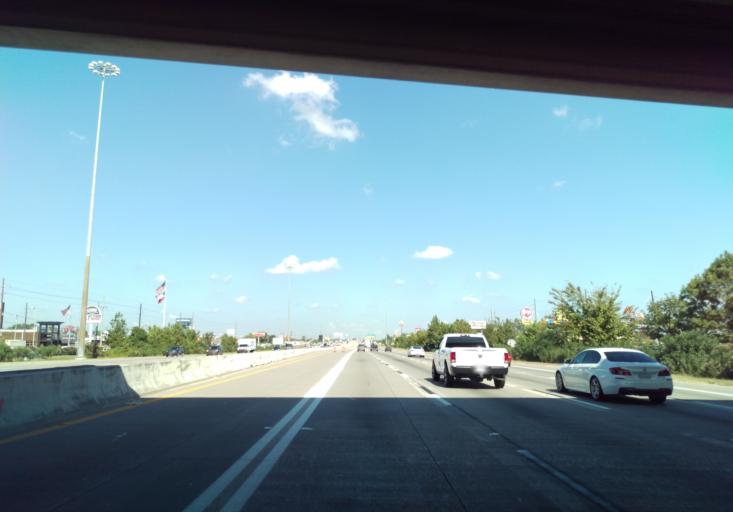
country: US
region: Texas
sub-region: Harris County
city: Spring
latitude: 30.0665
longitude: -95.4343
